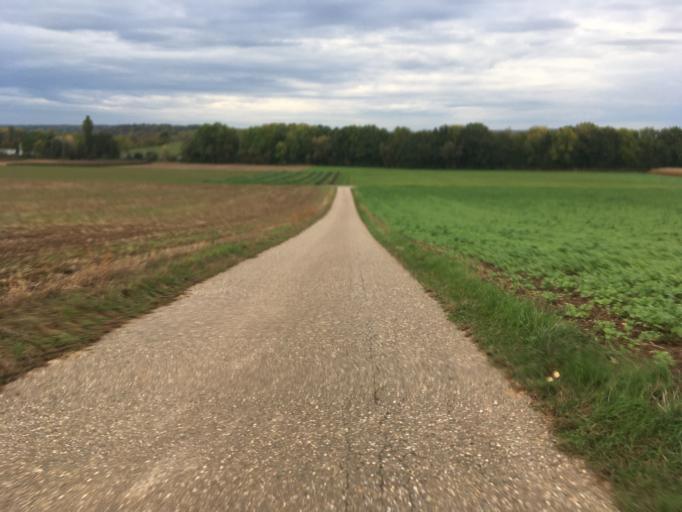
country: DE
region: Baden-Wuerttemberg
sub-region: Regierungsbezirk Stuttgart
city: Brackenheim
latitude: 49.0647
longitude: 9.0497
